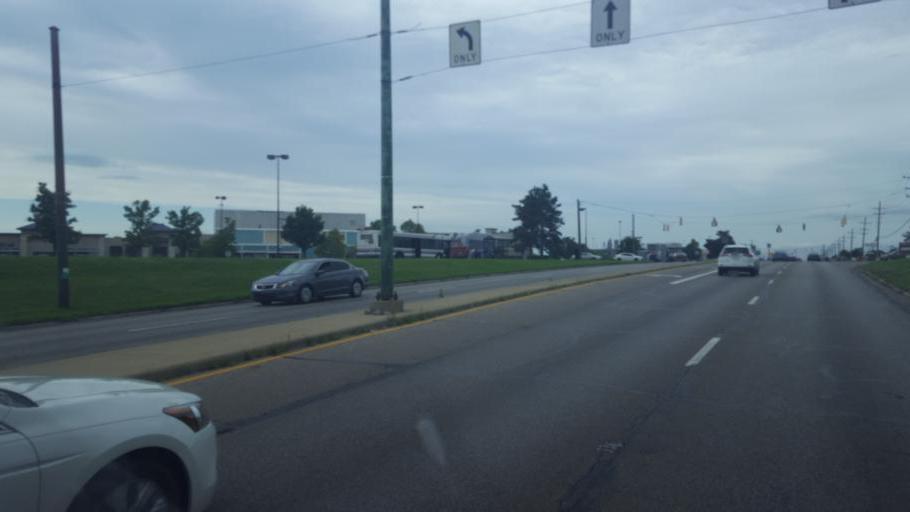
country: US
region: Ohio
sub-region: Franklin County
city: Blacklick Estates
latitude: 39.9179
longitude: -82.8803
